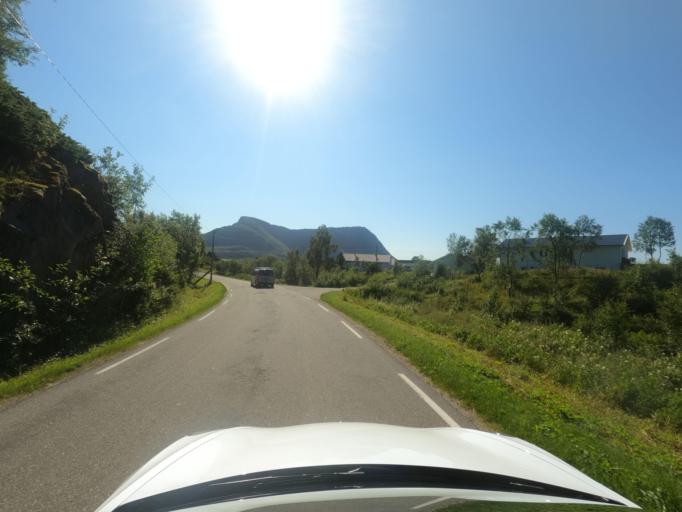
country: NO
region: Nordland
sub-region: Hadsel
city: Stokmarknes
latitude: 68.3112
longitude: 14.9870
